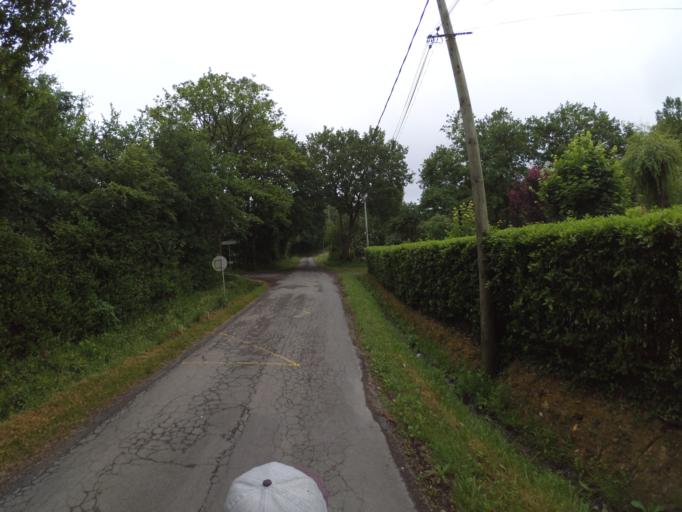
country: FR
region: Pays de la Loire
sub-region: Departement de la Vendee
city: La Roche-sur-Yon
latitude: 46.6306
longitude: -1.4253
